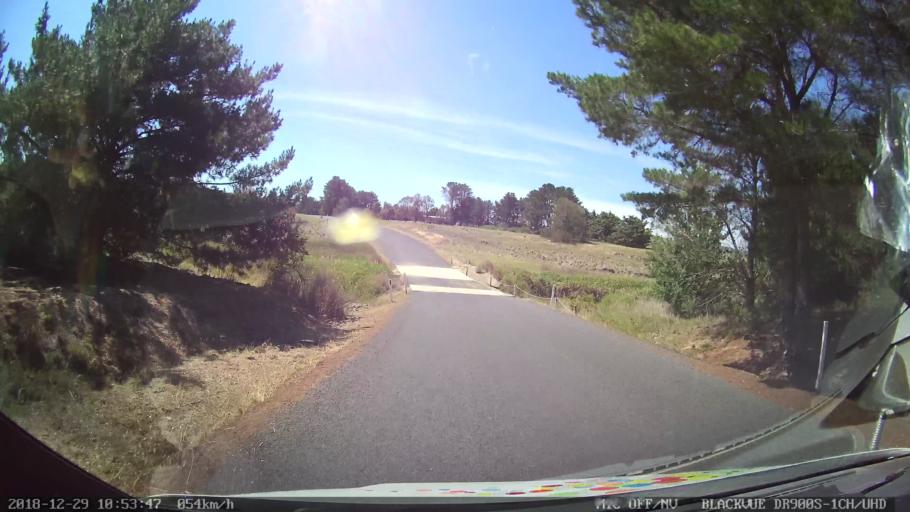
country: AU
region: New South Wales
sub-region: Palerang
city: Bungendore
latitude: -35.1120
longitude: 149.5218
